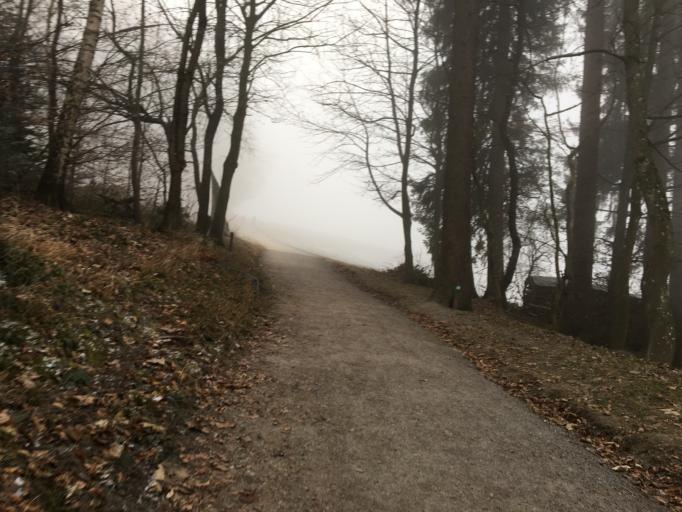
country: CH
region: Zurich
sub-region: Bezirk Horgen
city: Adliswil / Sonnenberg
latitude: 47.3064
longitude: 8.5080
